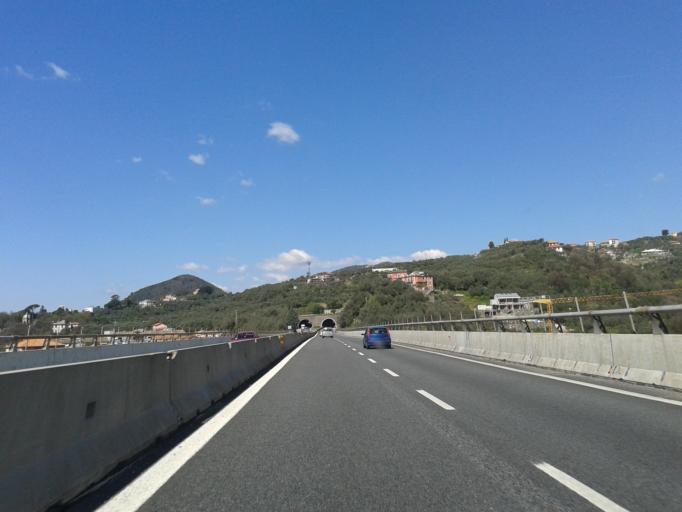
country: IT
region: Liguria
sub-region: Provincia di Genova
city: San Salvatore
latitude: 44.3200
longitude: 9.3439
